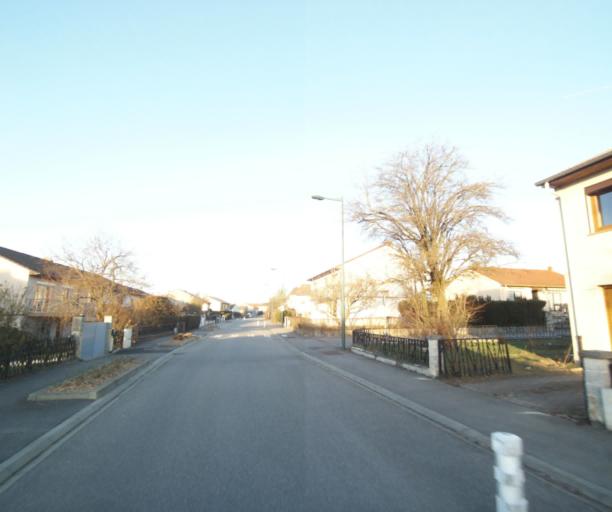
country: FR
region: Lorraine
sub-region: Departement de Meurthe-et-Moselle
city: Saulxures-les-Nancy
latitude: 48.6873
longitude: 6.2365
